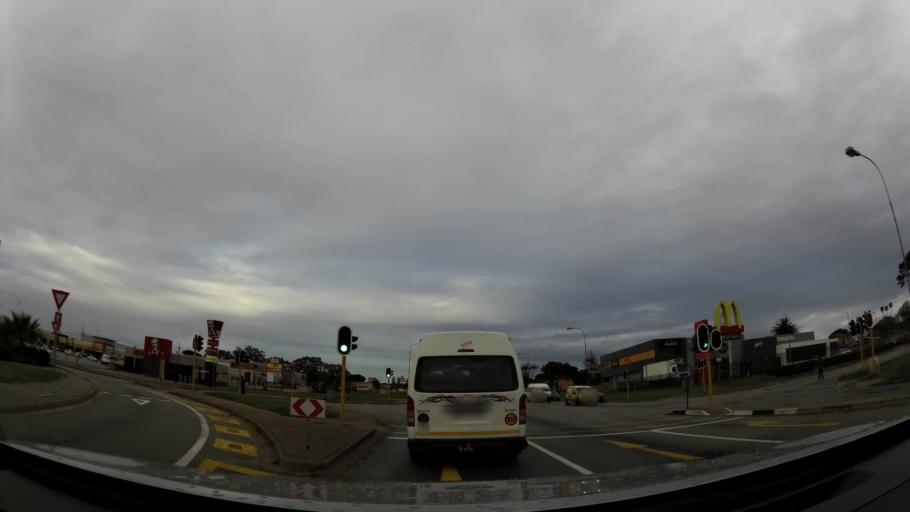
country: ZA
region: Eastern Cape
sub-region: Nelson Mandela Bay Metropolitan Municipality
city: Port Elizabeth
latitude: -33.9837
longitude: 25.5531
